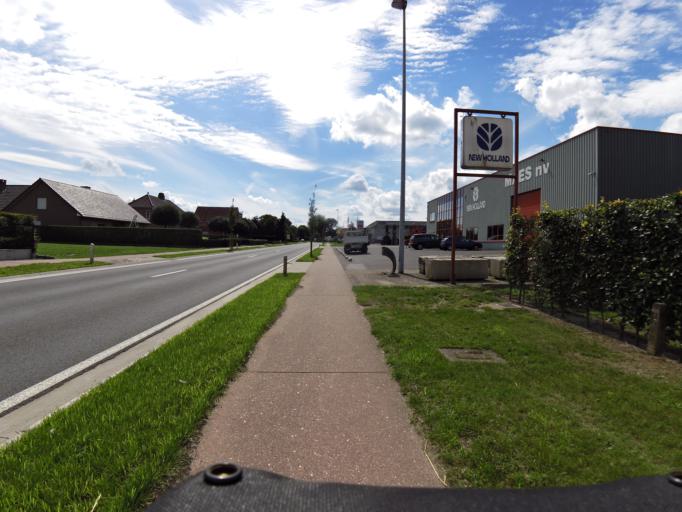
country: BE
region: Flanders
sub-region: Provincie Antwerpen
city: Hoogstraten
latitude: 51.4276
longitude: 4.7609
